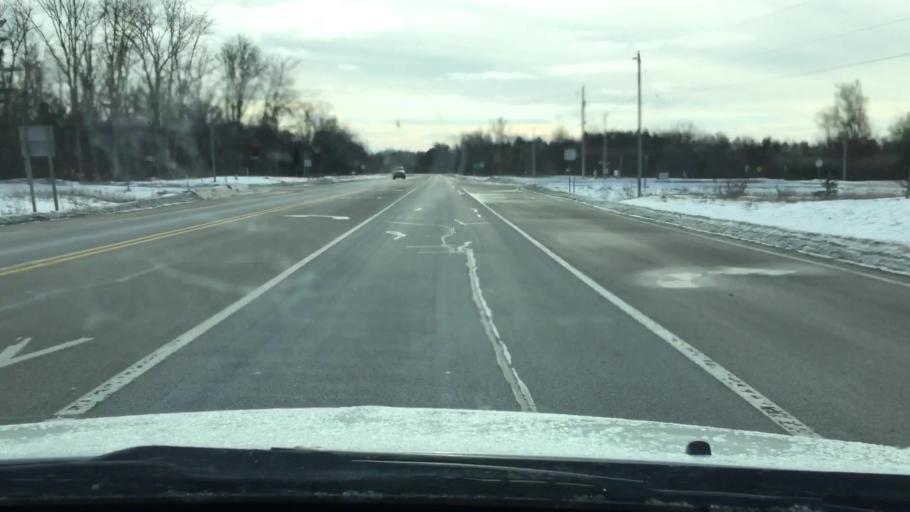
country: US
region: Michigan
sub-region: Wexford County
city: Manton
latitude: 44.5130
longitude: -85.4011
